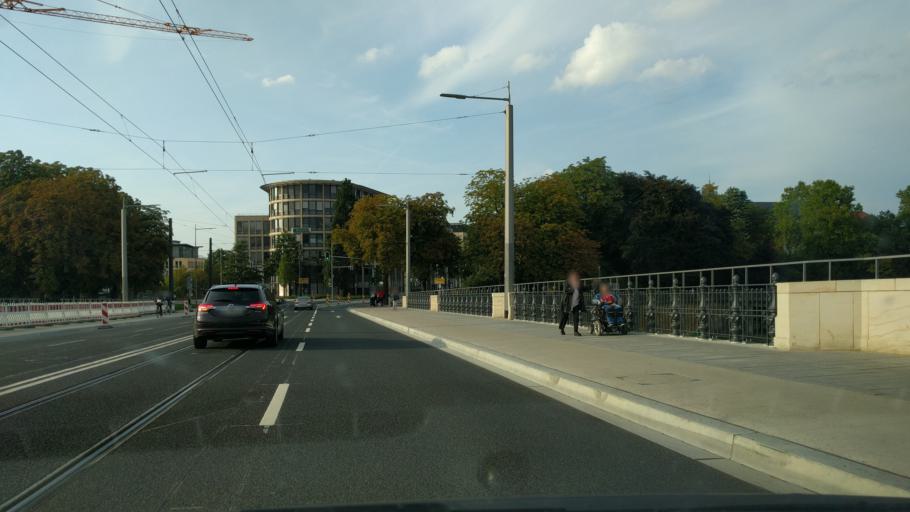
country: DE
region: Saxony
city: Dresden
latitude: 51.0578
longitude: 13.7539
